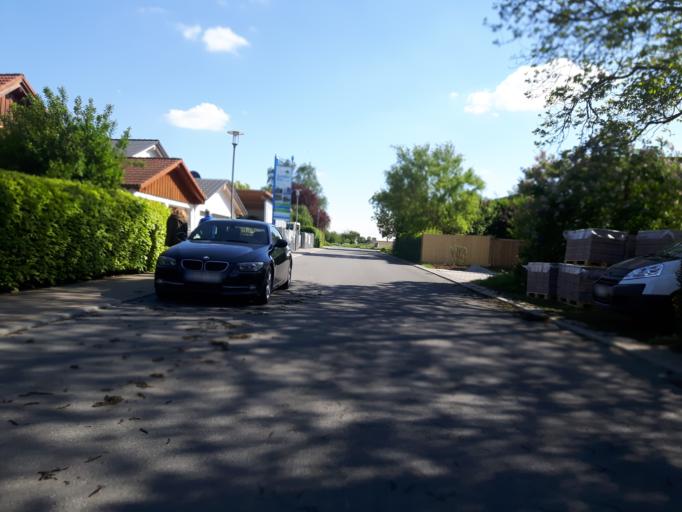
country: DE
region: Baden-Wuerttemberg
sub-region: Regierungsbezirk Stuttgart
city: Gundelsheim
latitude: 49.2736
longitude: 9.1600
